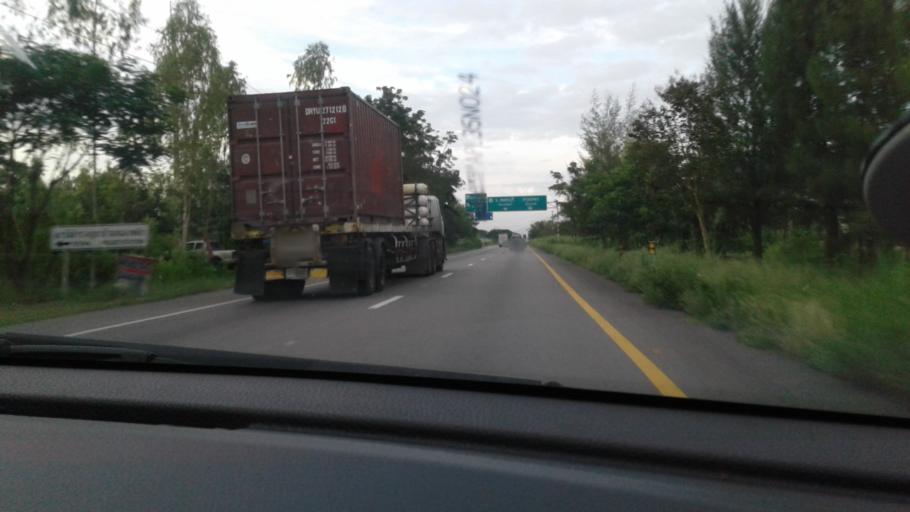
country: TH
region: Prachuap Khiri Khan
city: Hua Hin
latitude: 12.5693
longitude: 99.8680
